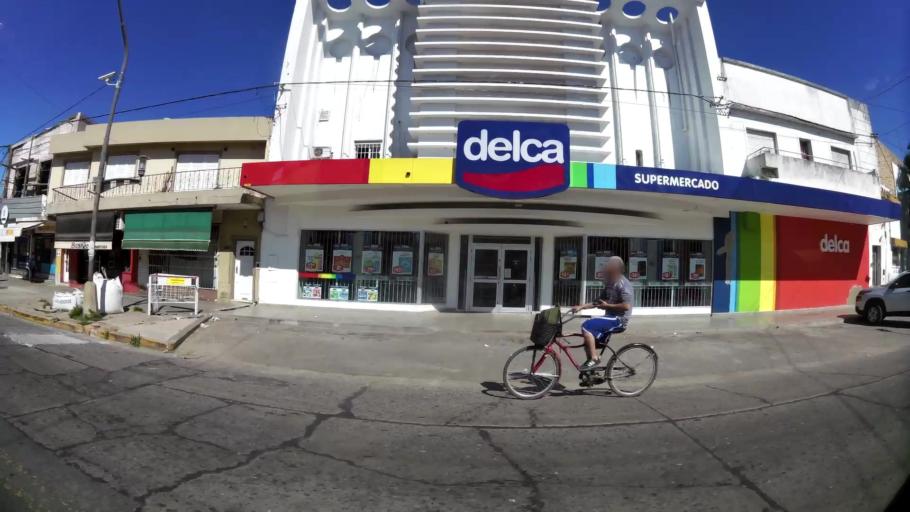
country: AR
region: Santa Fe
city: Santa Fe de la Vera Cruz
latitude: -31.6209
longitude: -60.6863
